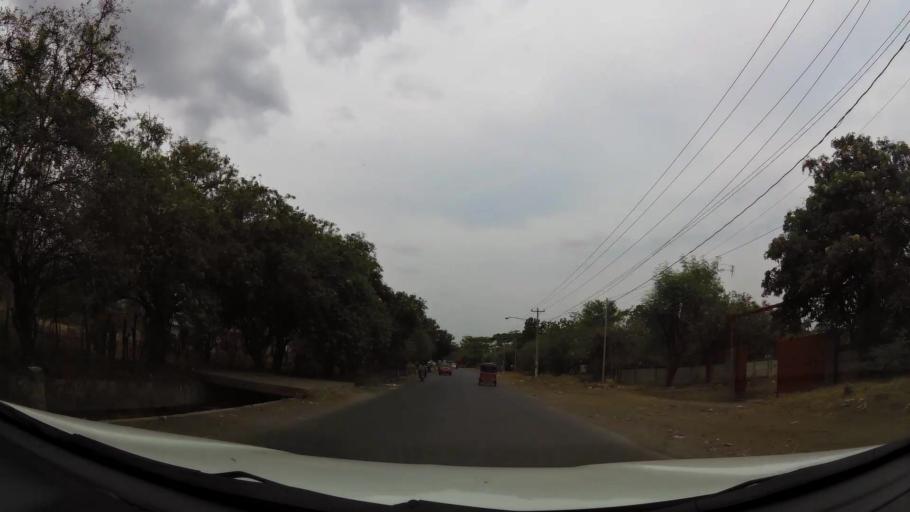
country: NI
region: Managua
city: Managua
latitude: 12.1249
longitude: -86.1778
